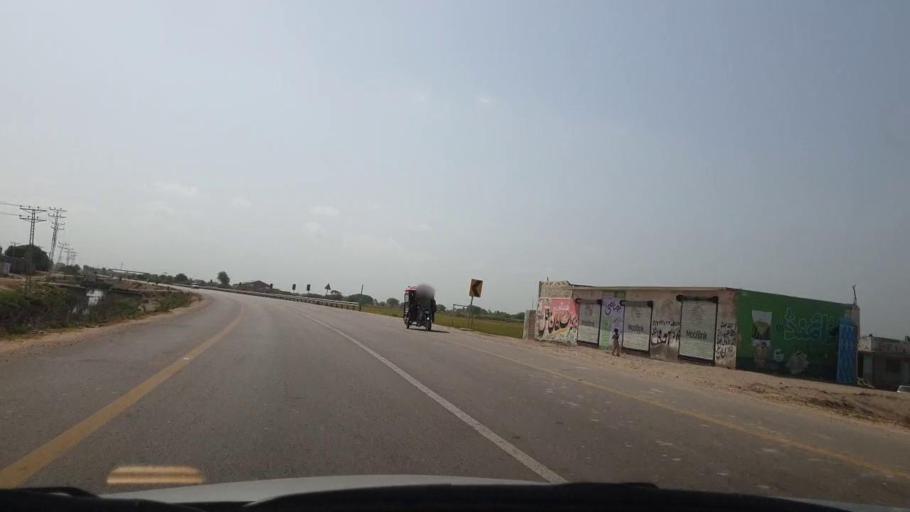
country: PK
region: Sindh
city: Matli
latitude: 25.0030
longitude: 68.6501
